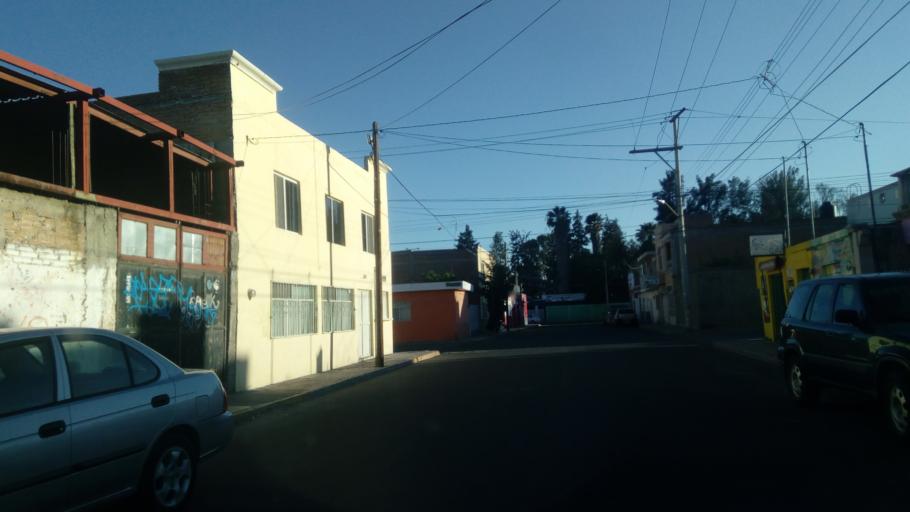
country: MX
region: Durango
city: Victoria de Durango
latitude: 24.0062
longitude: -104.6774
